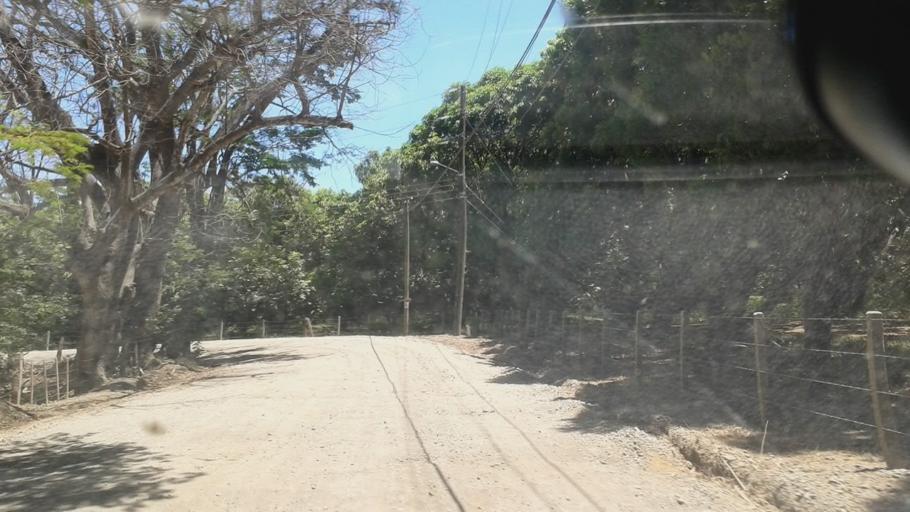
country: CR
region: Guanacaste
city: Samara
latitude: 9.9923
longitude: -85.6743
